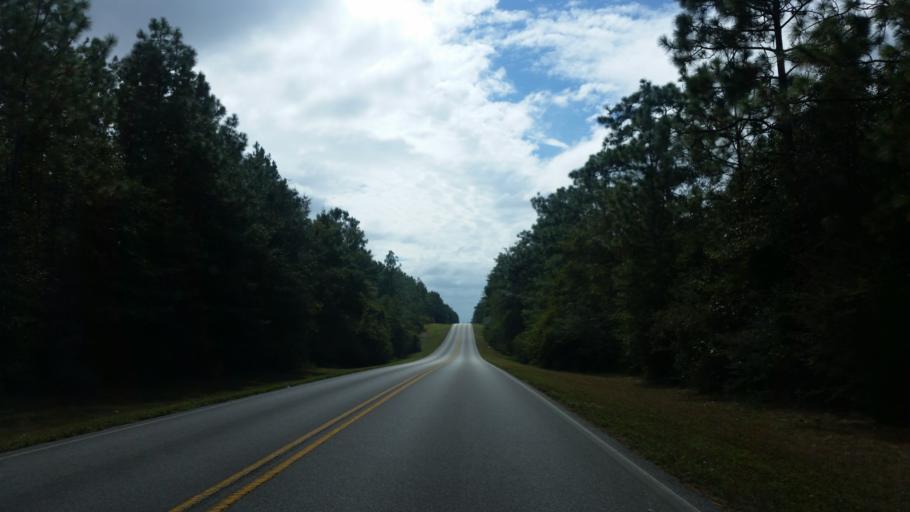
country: US
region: Florida
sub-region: Santa Rosa County
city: Point Baker
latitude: 30.7398
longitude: -86.9477
